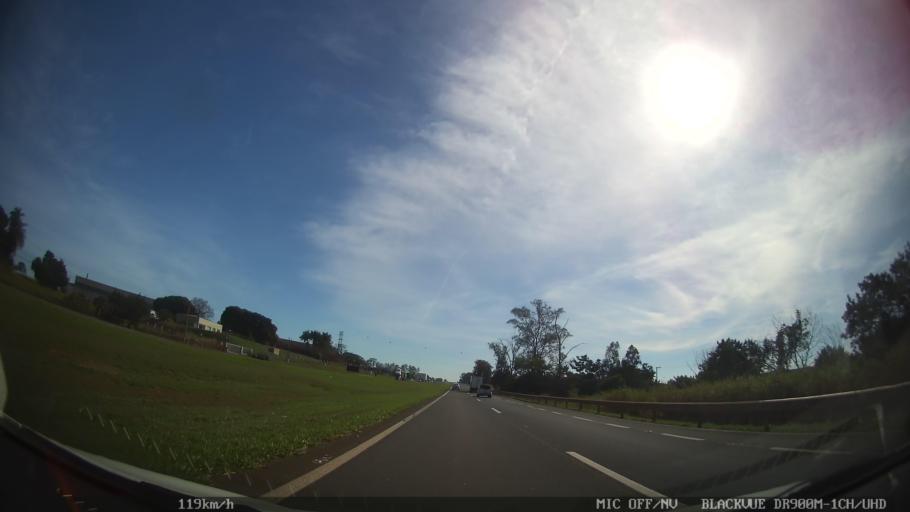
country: BR
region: Sao Paulo
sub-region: Leme
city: Leme
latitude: -22.2157
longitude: -47.3930
